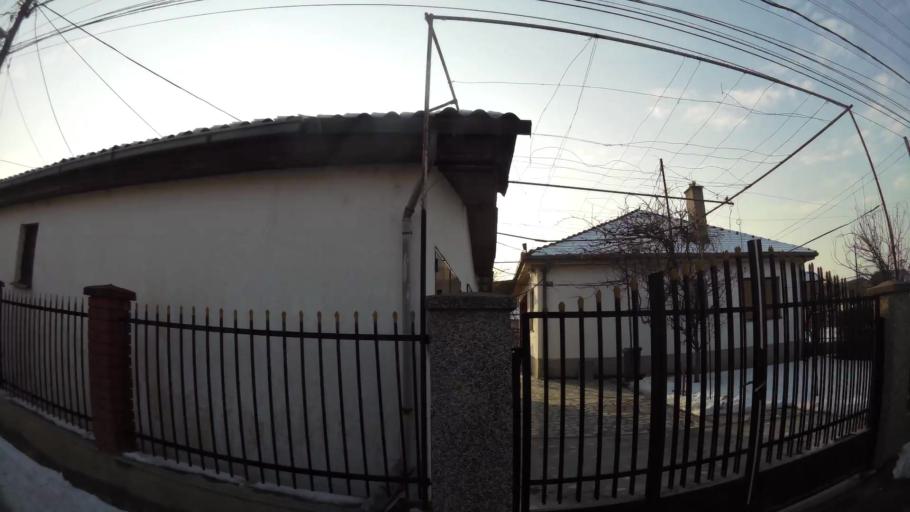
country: MK
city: Creshevo
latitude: 42.0235
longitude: 21.5203
